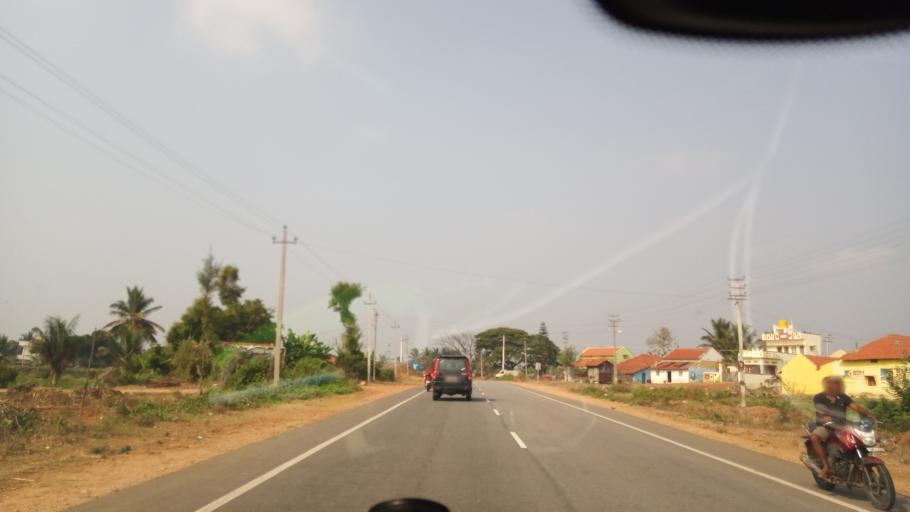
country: IN
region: Karnataka
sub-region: Mandya
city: Nagamangala
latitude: 12.7343
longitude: 76.7195
